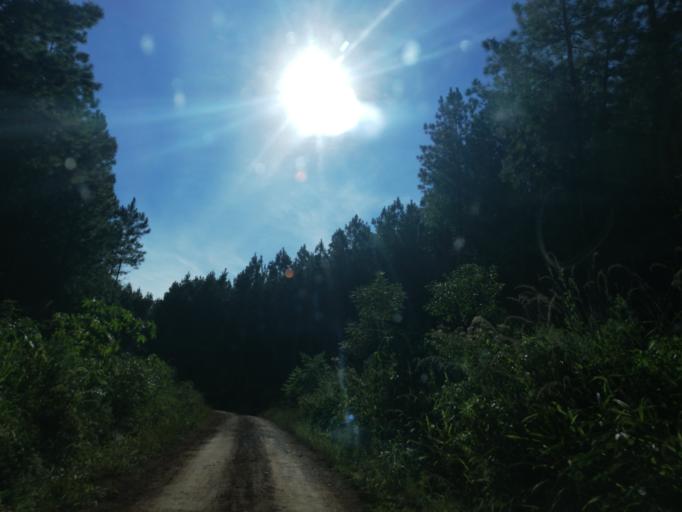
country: AR
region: Misiones
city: Dos de Mayo
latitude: -27.0152
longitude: -54.4416
